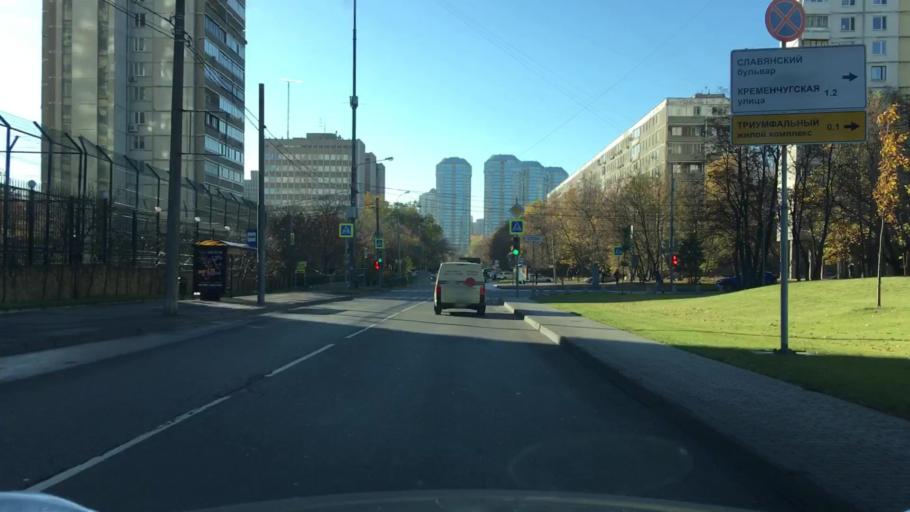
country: RU
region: Moscow
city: Davydkovo
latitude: 55.7277
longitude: 37.4787
